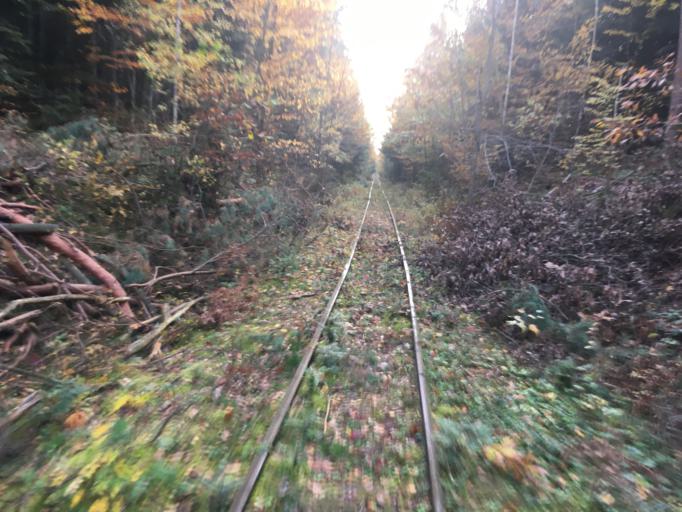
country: PL
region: Swietokrzyskie
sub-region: Powiat starachowicki
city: Brody
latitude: 51.0749
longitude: 21.1506
